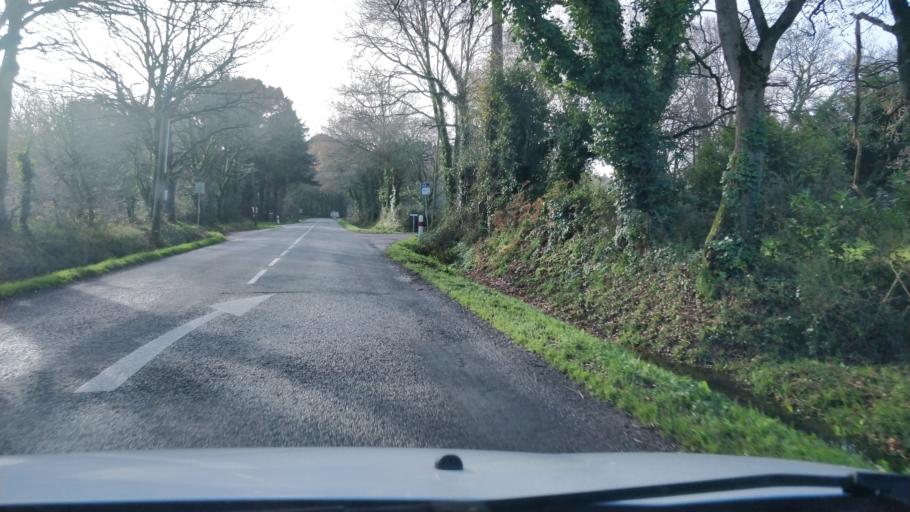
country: FR
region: Pays de la Loire
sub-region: Departement de la Loire-Atlantique
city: Saint-Molf
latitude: 47.3741
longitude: -2.4329
